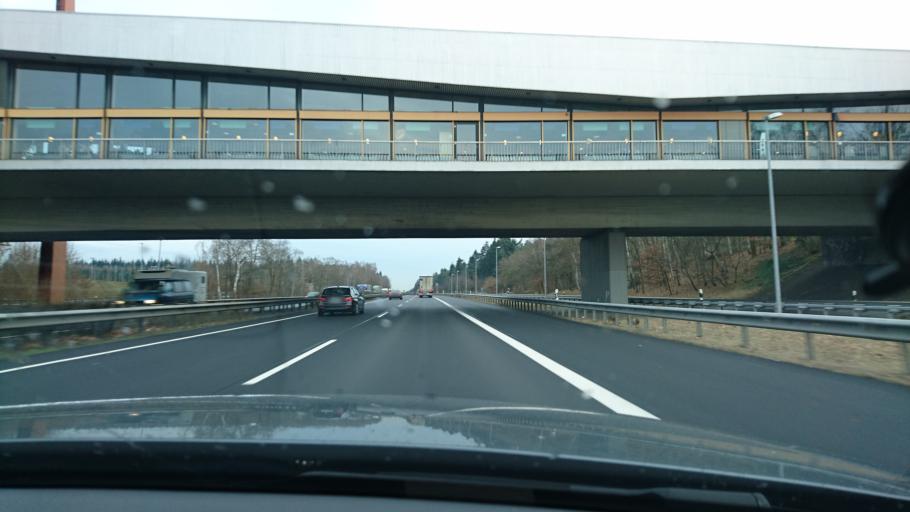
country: DE
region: Lower Saxony
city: Holdorf
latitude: 52.5394
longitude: 8.1136
